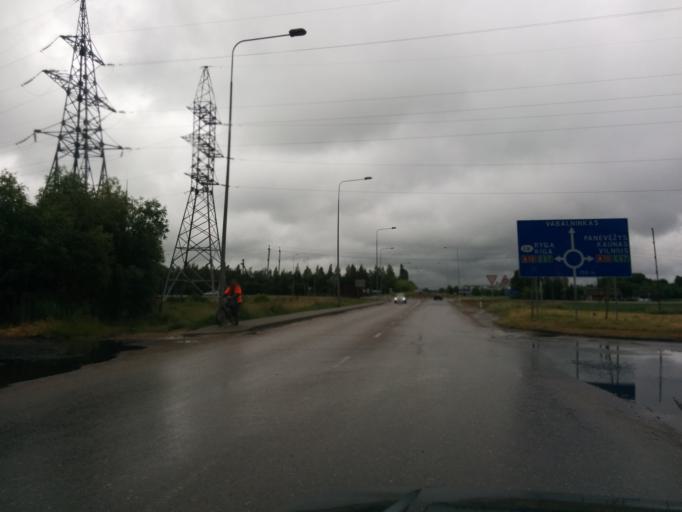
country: LT
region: Panevezys
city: Pasvalys
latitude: 56.0563
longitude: 24.4079
